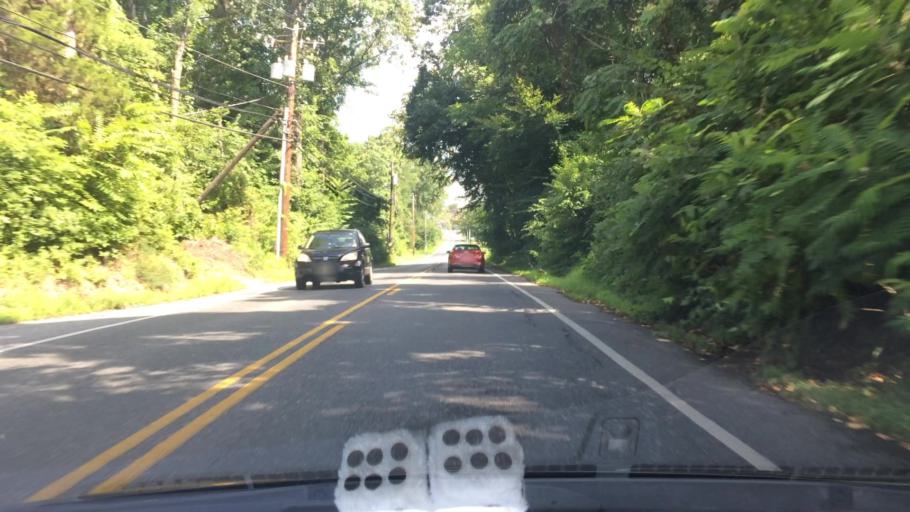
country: US
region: New Jersey
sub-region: Camden County
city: Blackwood
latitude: 39.7922
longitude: -75.0800
